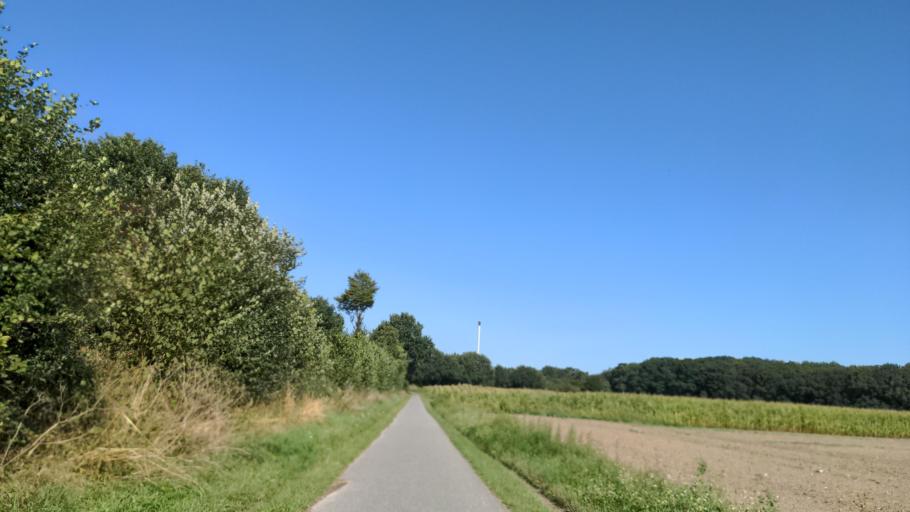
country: DE
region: Schleswig-Holstein
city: Klempau
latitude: 53.7699
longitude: 10.6621
